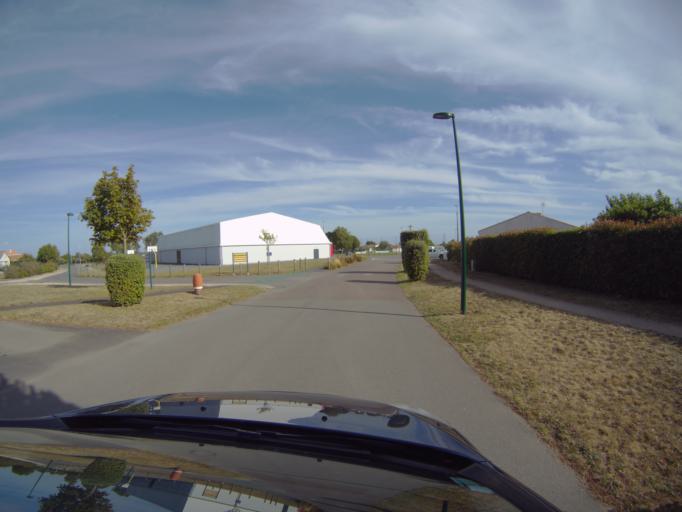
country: FR
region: Pays de la Loire
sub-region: Departement de la Vendee
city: Angles
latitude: 46.4087
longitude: -1.3948
